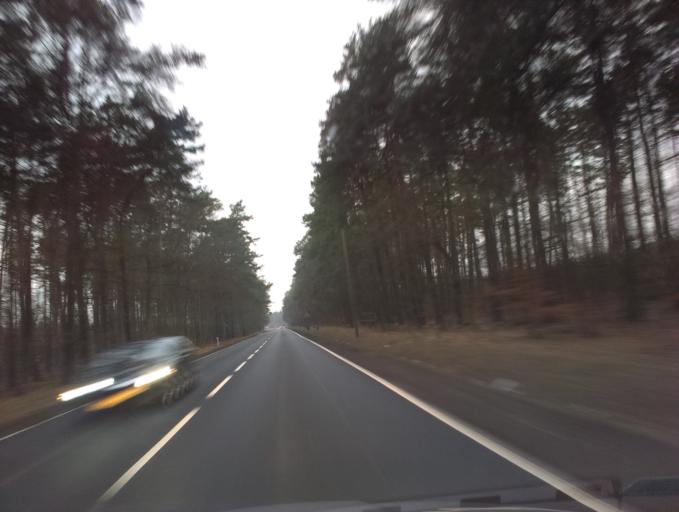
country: PL
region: Greater Poland Voivodeship
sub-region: Powiat zlotowski
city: Jastrowie
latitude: 53.3904
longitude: 16.7880
